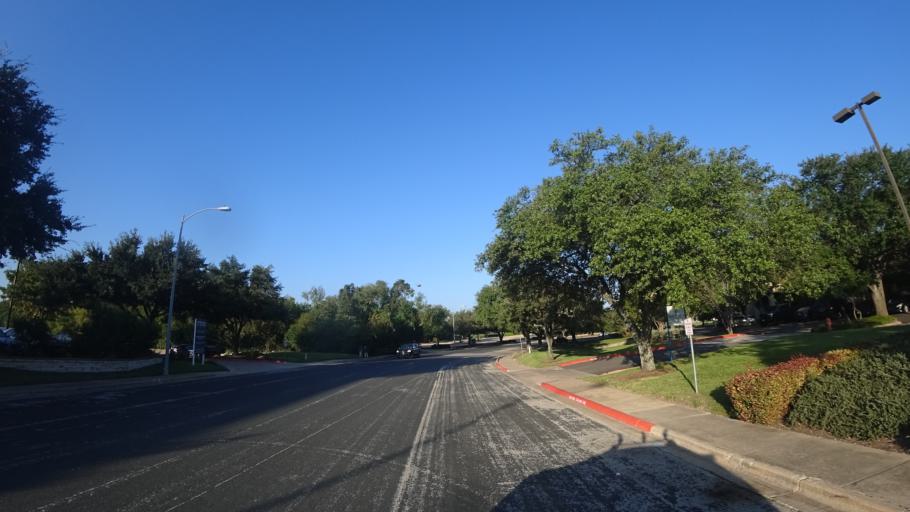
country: US
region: Texas
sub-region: Travis County
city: Austin
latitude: 30.3281
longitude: -97.6725
